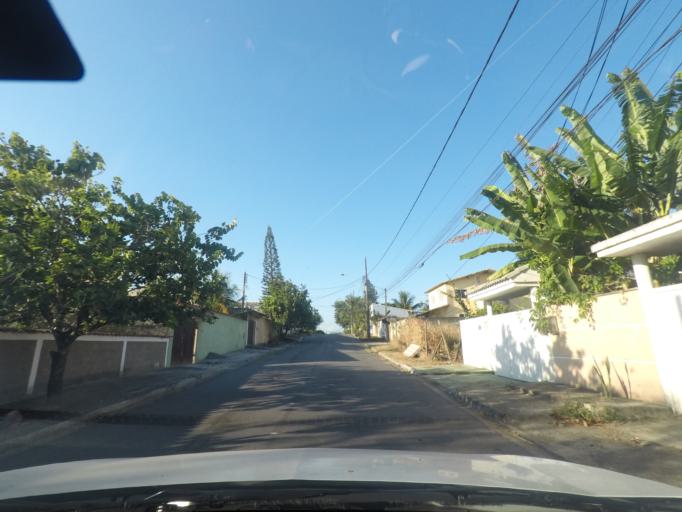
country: BR
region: Rio de Janeiro
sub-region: Marica
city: Marica
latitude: -22.9688
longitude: -42.9351
